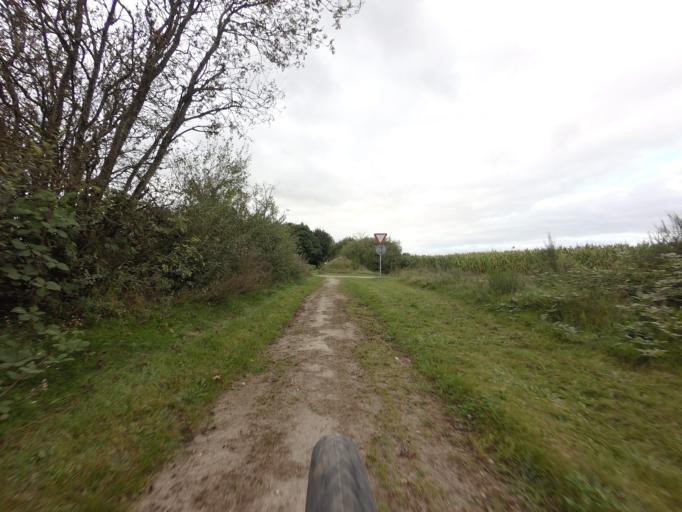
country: DK
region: South Denmark
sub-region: Billund Kommune
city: Billund
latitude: 55.8289
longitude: 9.0306
